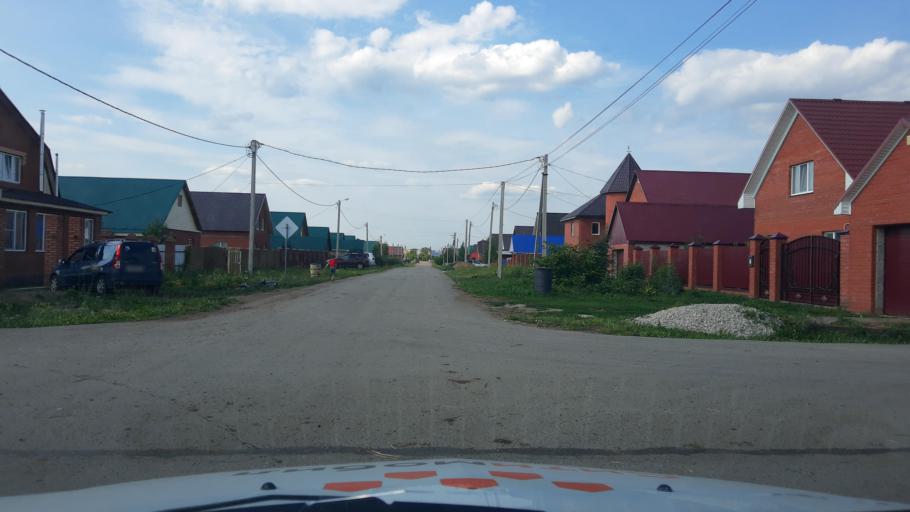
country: RU
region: Bashkortostan
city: Kabakovo
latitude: 54.6610
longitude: 56.2123
